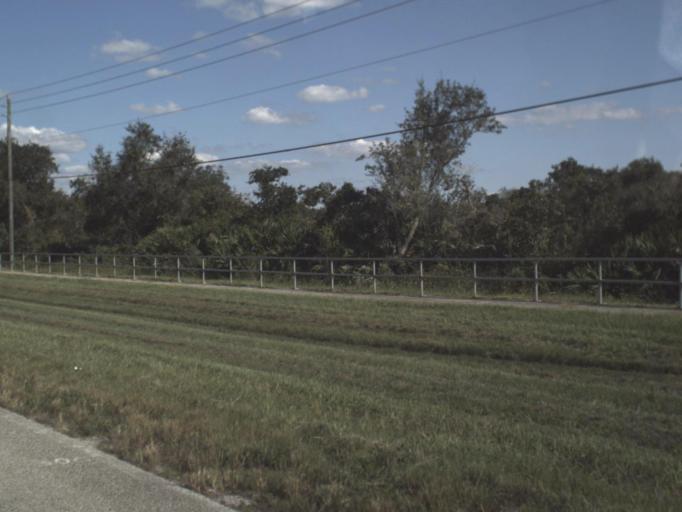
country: US
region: Florida
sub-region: Sarasota County
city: North Port
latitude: 26.9979
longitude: -82.1898
